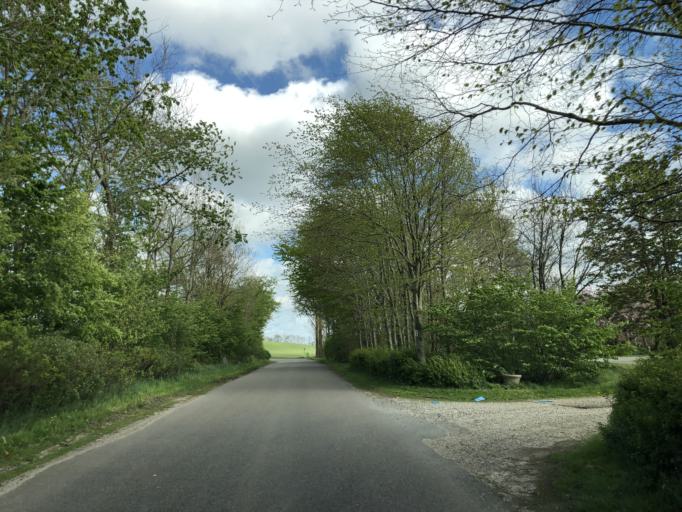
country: DK
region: Central Jutland
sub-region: Herning Kommune
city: Avlum
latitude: 56.3035
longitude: 8.7637
